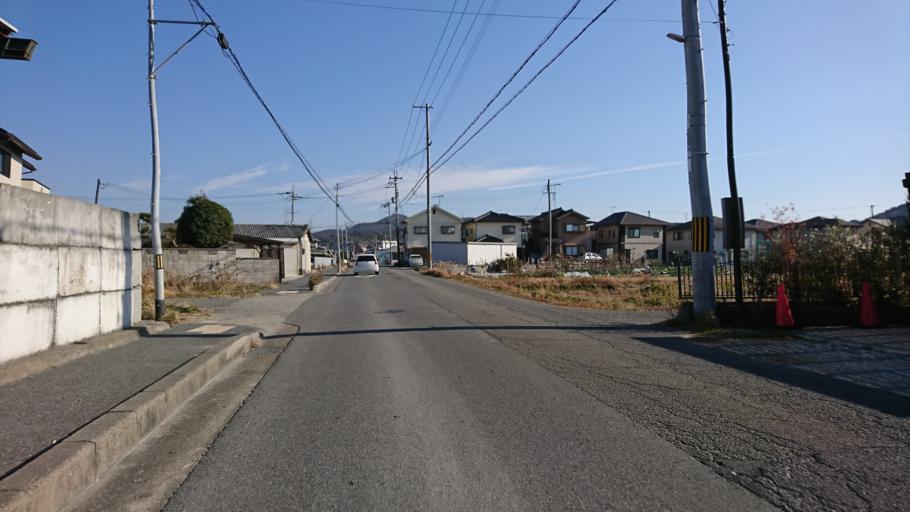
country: JP
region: Hyogo
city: Kakogawacho-honmachi
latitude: 34.8156
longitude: 134.8268
